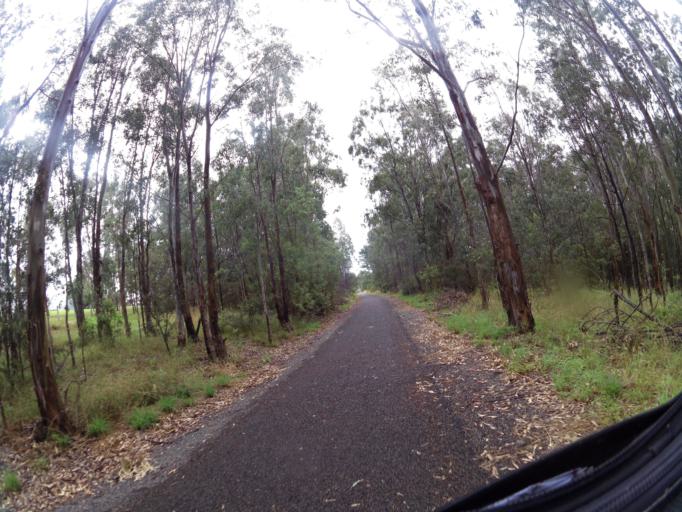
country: AU
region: Victoria
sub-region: East Gippsland
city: Bairnsdale
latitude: -37.8150
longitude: 147.7324
